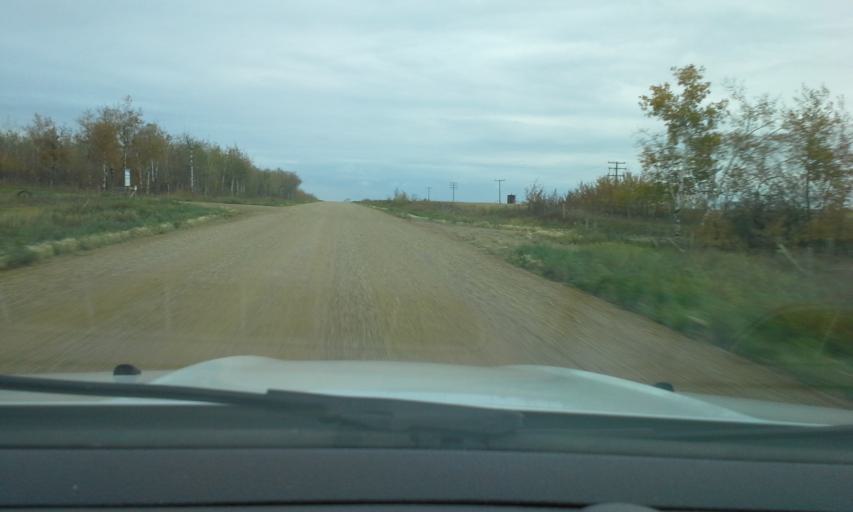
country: CA
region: Saskatchewan
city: Lloydminster
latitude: 53.2849
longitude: -109.8084
